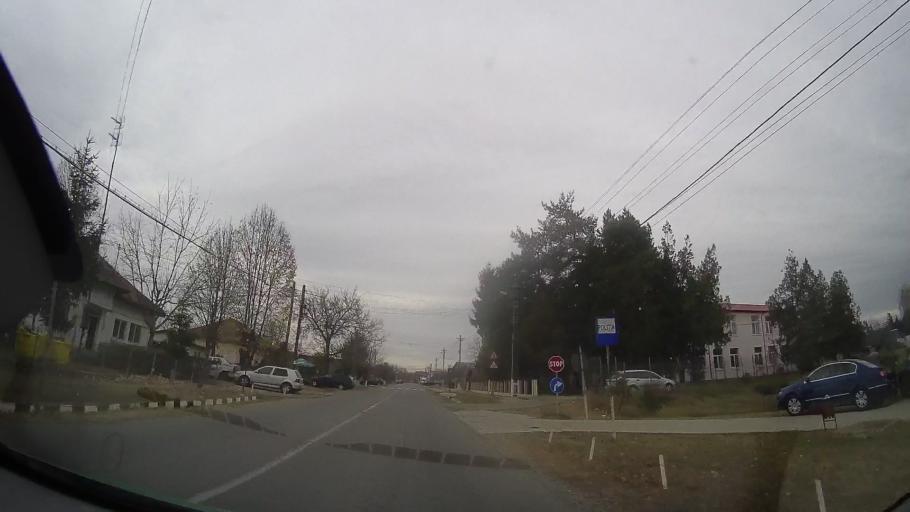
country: RO
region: Prahova
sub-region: Comuna Iordachianu
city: Iordacheanu
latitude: 45.0438
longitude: 26.2381
